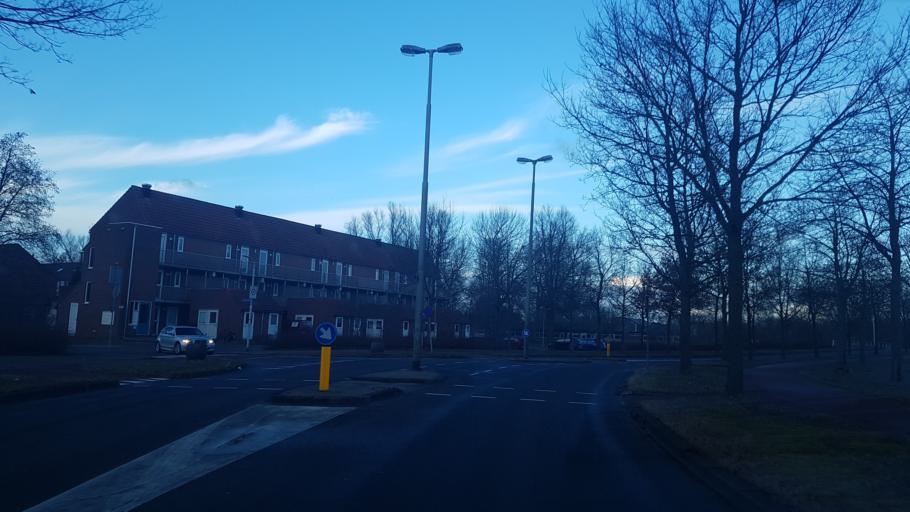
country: NL
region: Friesland
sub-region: Gemeente Leeuwarden
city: Camminghaburen
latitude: 53.2126
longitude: 5.8384
